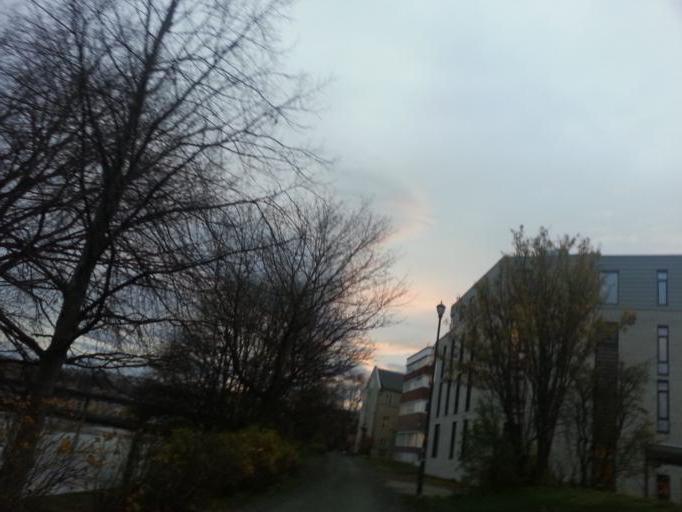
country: NO
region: Sor-Trondelag
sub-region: Trondheim
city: Trondheim
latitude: 63.4238
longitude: 10.3888
